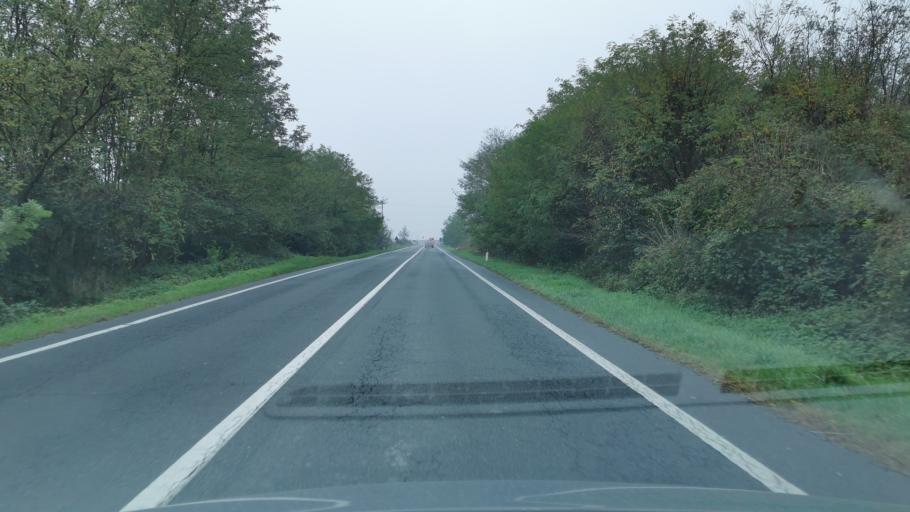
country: IT
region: Piedmont
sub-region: Provincia di Torino
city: Strambino
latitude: 45.3835
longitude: 7.8991
